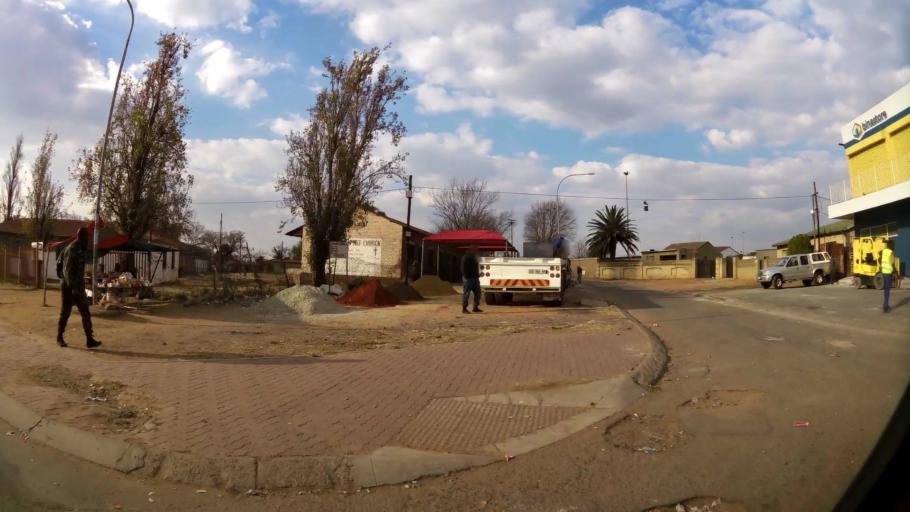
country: ZA
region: Gauteng
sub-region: City of Johannesburg Metropolitan Municipality
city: Soweto
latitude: -26.2320
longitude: 27.9258
